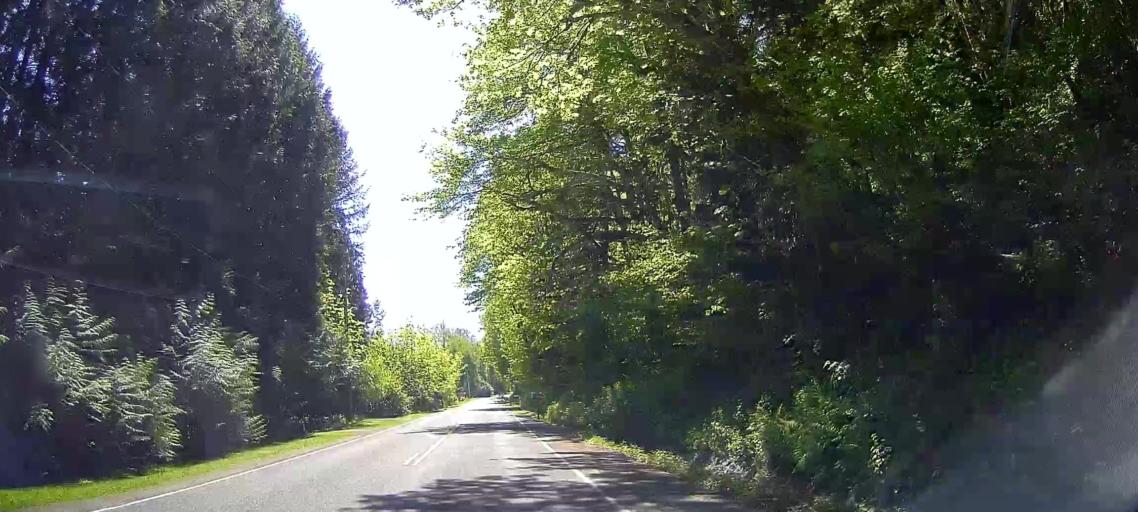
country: US
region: Washington
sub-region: Snohomish County
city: Darrington
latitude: 48.5056
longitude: -121.6652
